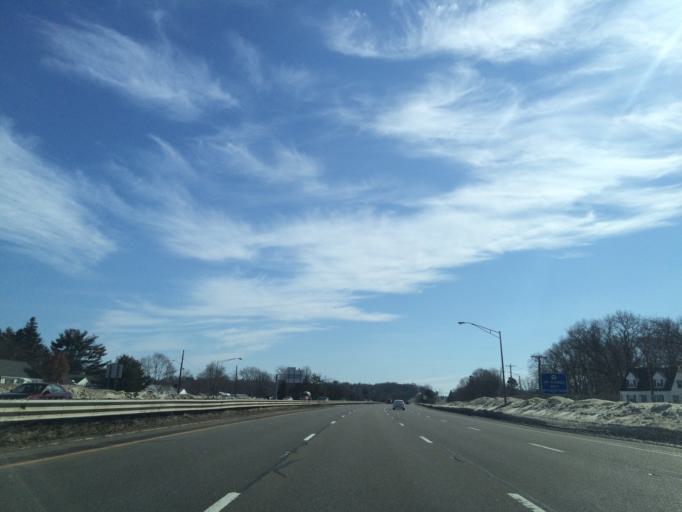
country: US
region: Massachusetts
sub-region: Middlesex County
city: Belmont
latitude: 42.4170
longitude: -71.2005
